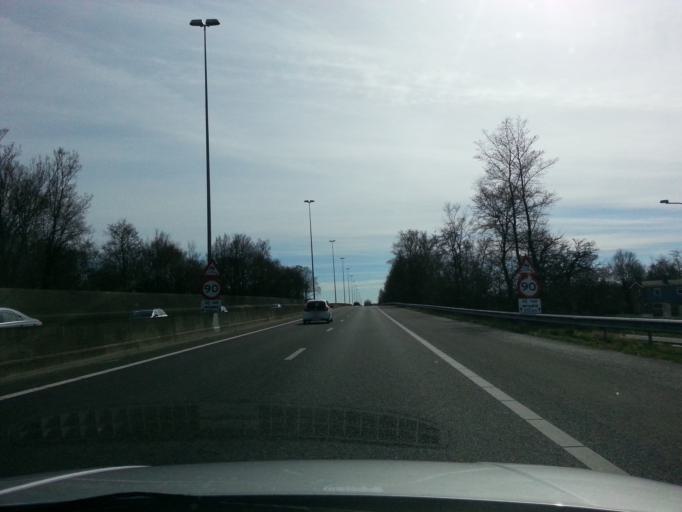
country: NL
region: Groningen
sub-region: Gemeente Haren
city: Haren
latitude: 53.1691
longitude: 6.5910
